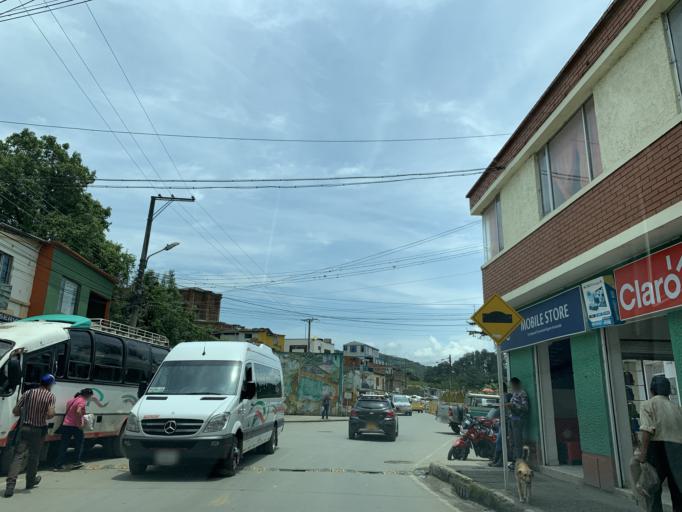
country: CO
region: Boyaca
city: Moniquira
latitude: 5.8778
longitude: -73.5697
